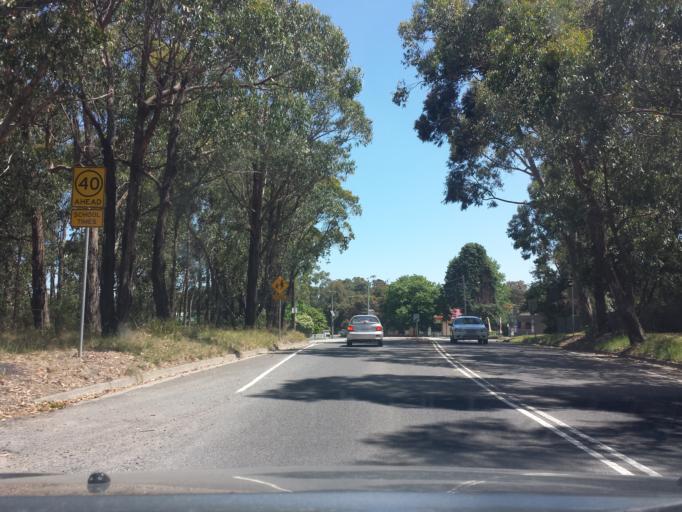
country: AU
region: Victoria
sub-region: Yarra Ranges
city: Belgrave Heights
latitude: -37.9300
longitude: 145.3608
